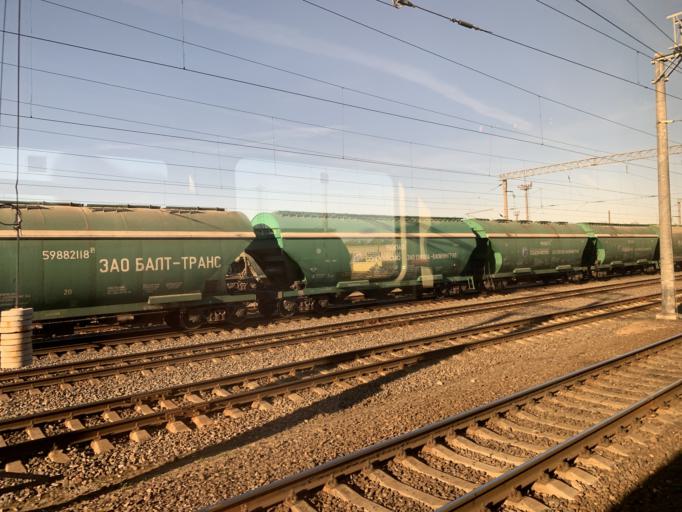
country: BY
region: Minsk
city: Maladzyechna
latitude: 54.3165
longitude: 26.8316
